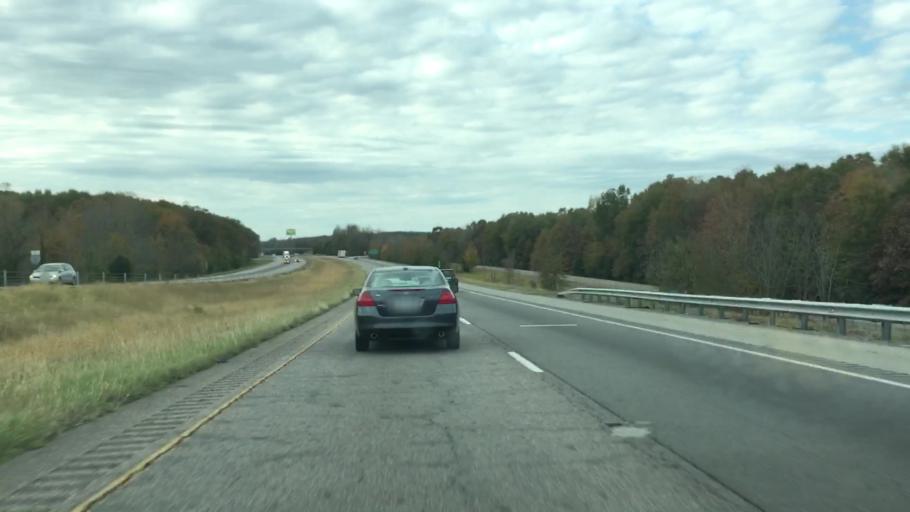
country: US
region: Arkansas
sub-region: Faulkner County
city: Conway
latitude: 35.1501
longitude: -92.5447
